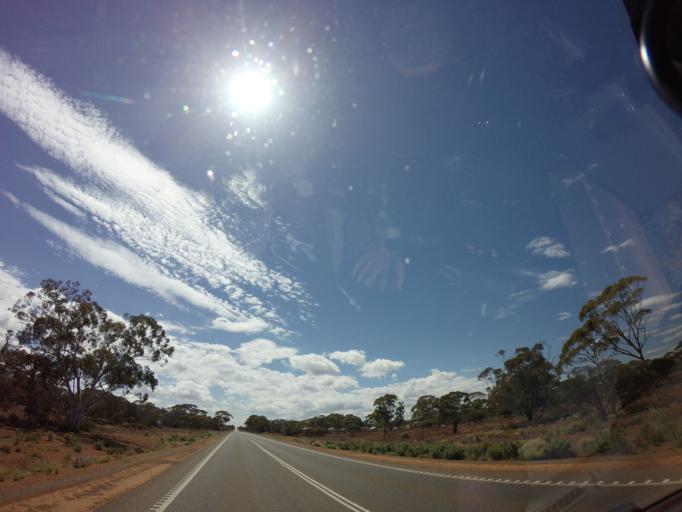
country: AU
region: Western Australia
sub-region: Kalgoorlie/Boulder
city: Boulder
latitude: -30.9546
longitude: 121.1430
